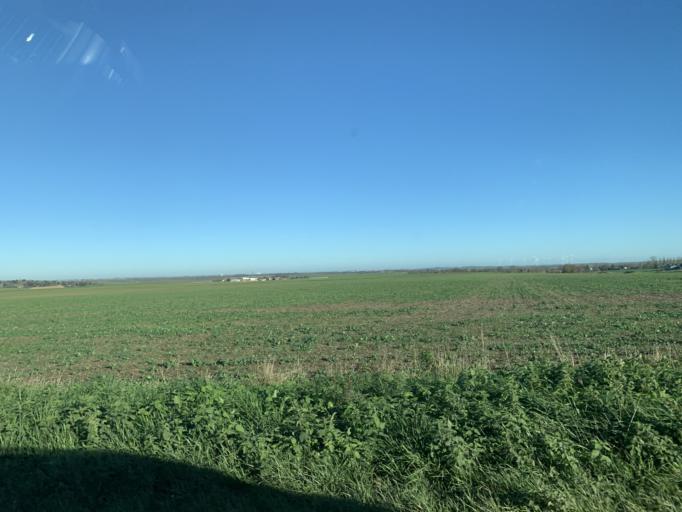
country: FR
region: Nord-Pas-de-Calais
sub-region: Departement du Nord
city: Escaudoeuvres
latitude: 50.1633
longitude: 3.2845
